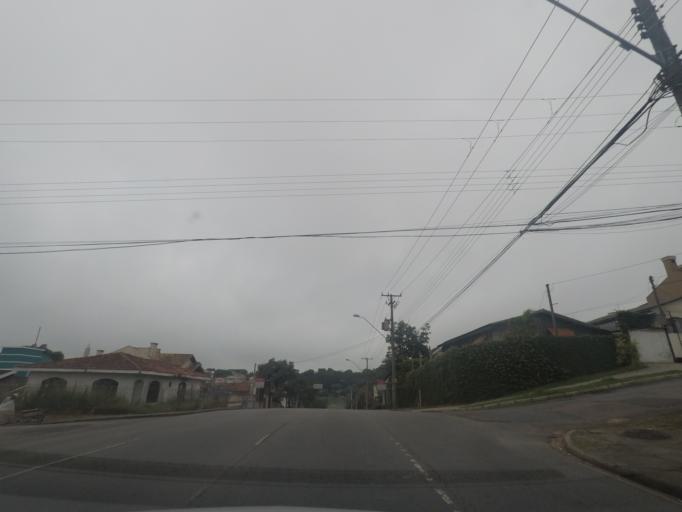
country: BR
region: Parana
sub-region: Curitiba
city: Curitiba
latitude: -25.3791
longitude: -49.2239
